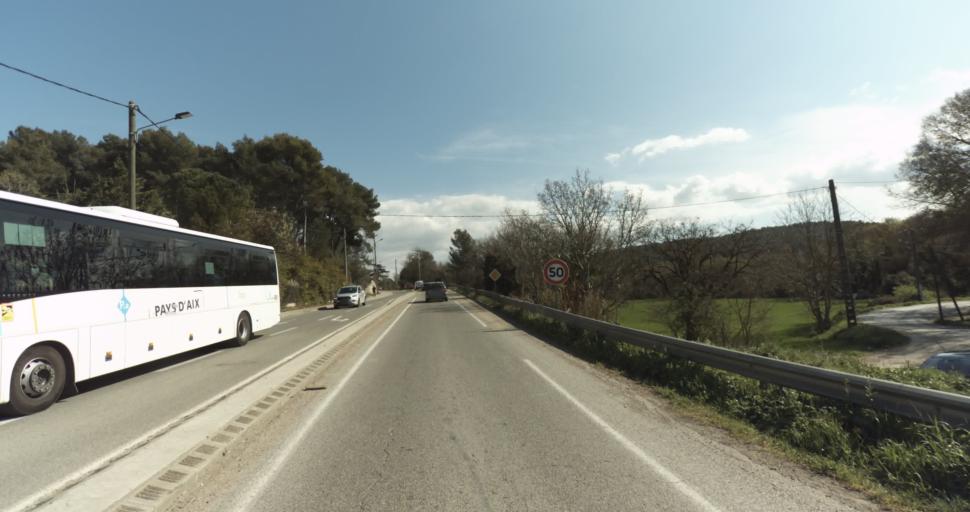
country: FR
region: Provence-Alpes-Cote d'Azur
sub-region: Departement des Bouches-du-Rhone
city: Bouc-Bel-Air
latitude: 43.4799
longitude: 5.4235
